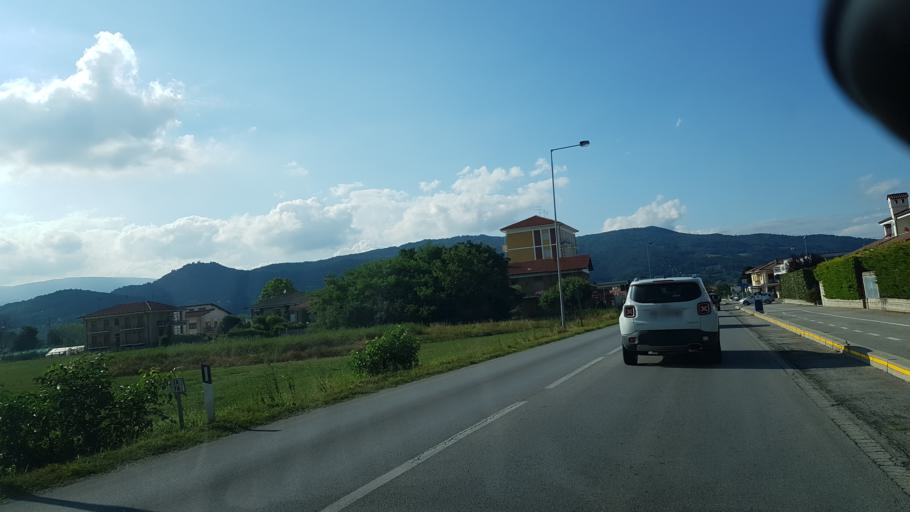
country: IT
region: Piedmont
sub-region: Provincia di Cuneo
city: Busca
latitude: 44.5062
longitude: 7.4876
